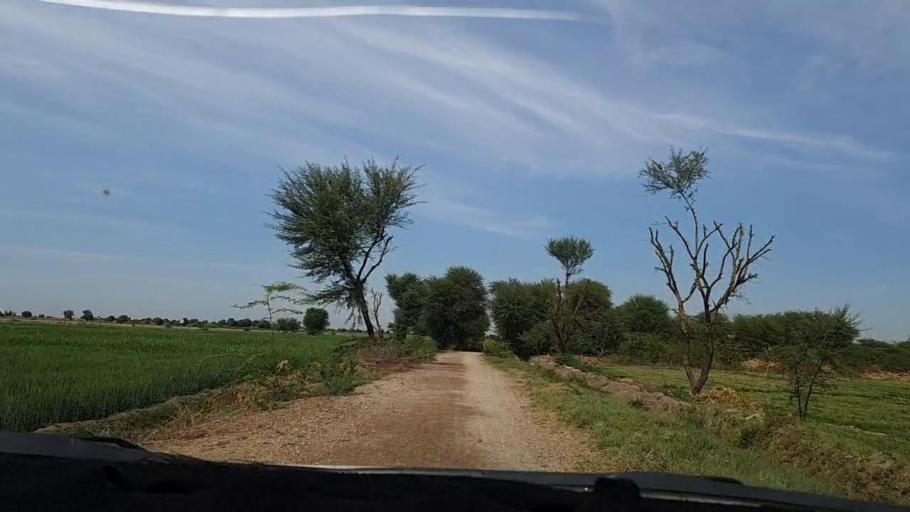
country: PK
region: Sindh
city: Dhoro Naro
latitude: 25.4596
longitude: 69.4775
